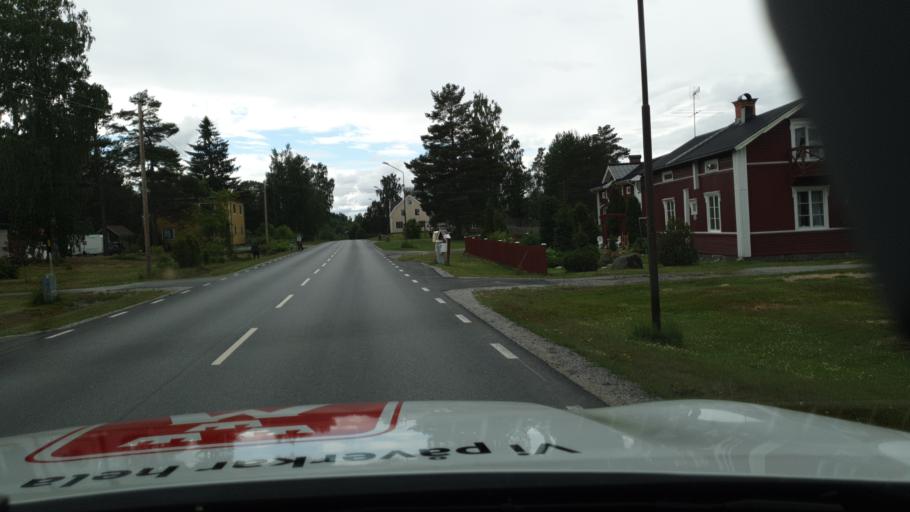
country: SE
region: Vaesterbotten
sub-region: Nordmalings Kommun
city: Nordmaling
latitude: 63.5548
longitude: 19.3972
